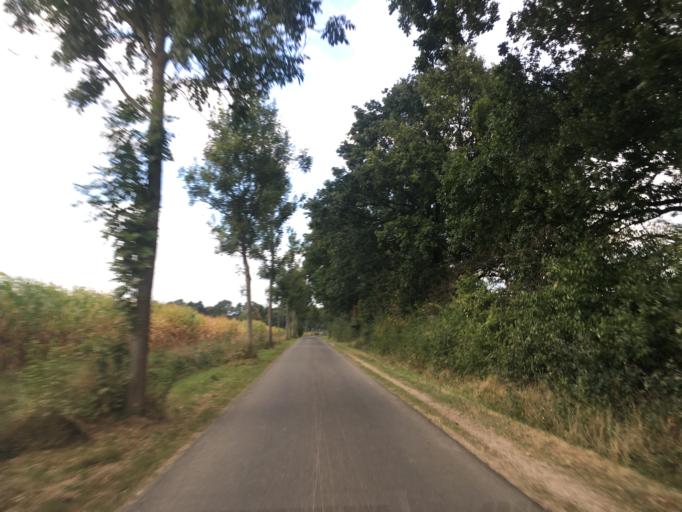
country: DE
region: North Rhine-Westphalia
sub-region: Regierungsbezirk Munster
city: Altenberge
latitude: 51.9784
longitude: 7.5306
